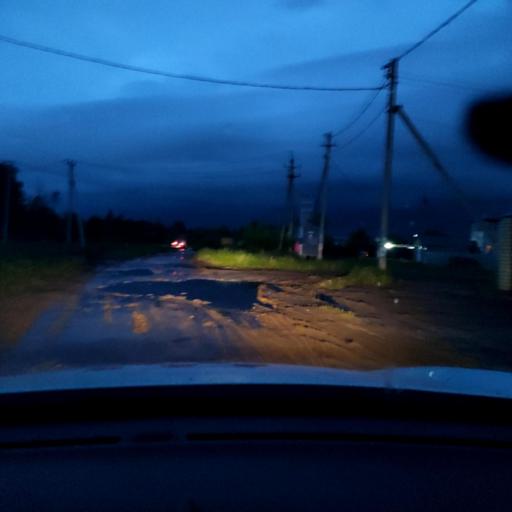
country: RU
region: Tatarstan
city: Stolbishchi
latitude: 55.6494
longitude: 49.2843
